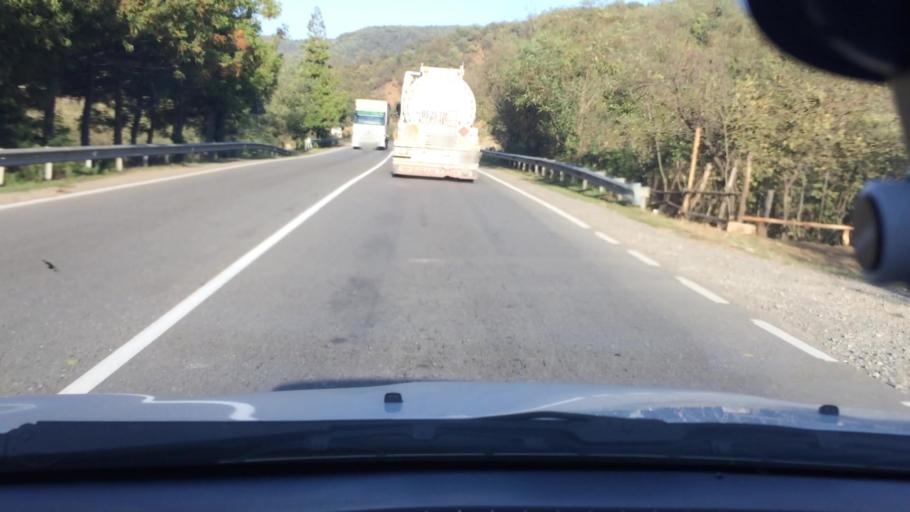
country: GE
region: Imereti
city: Kharagauli
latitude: 42.1083
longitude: 43.1849
